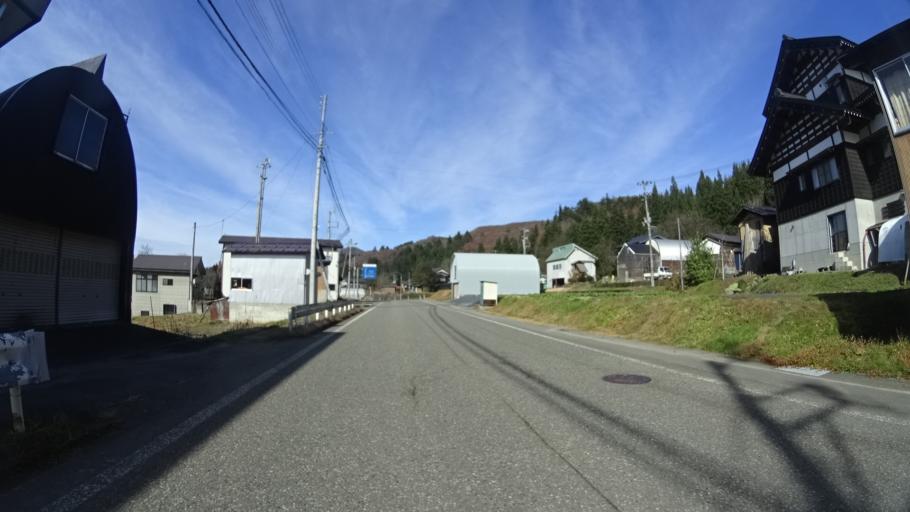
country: JP
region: Niigata
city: Muikamachi
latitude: 37.2019
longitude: 139.0750
